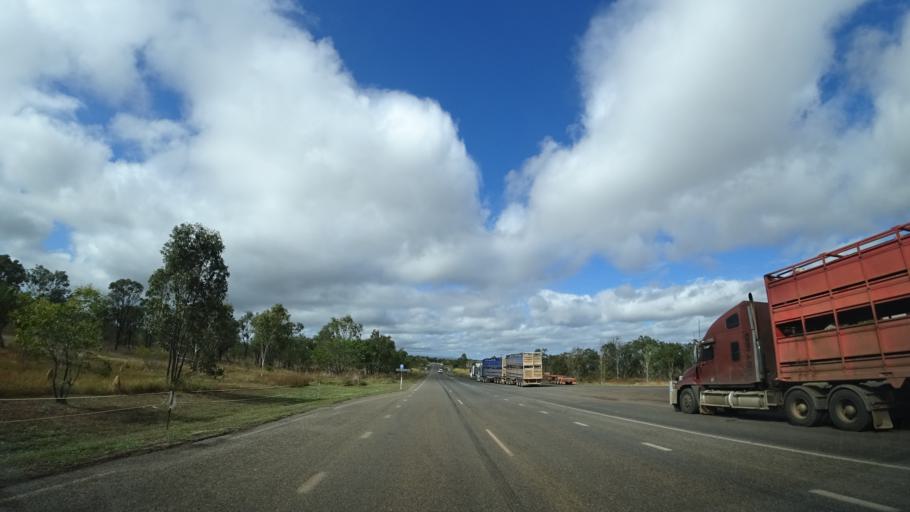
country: AU
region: Queensland
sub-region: Cook
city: Cooktown
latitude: -15.8638
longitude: 144.8585
